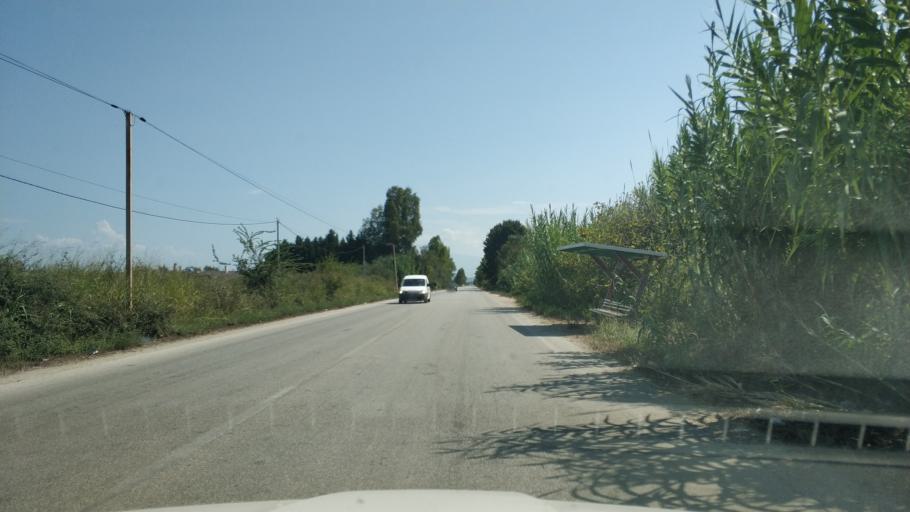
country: AL
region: Fier
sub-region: Rrethi i Lushnjes
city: Krutja e Poshtme
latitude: 40.8874
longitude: 19.6482
